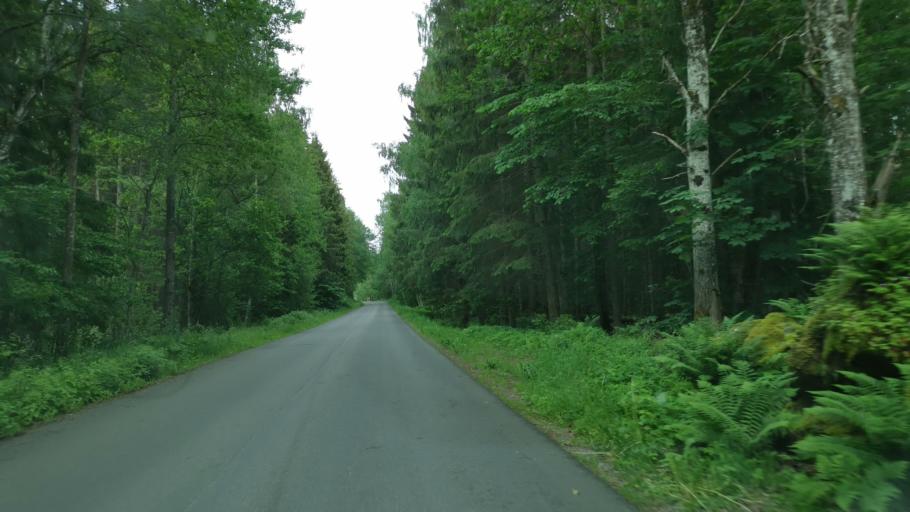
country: SE
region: Vaestra Goetaland
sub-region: Vanersborgs Kommun
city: Vargon
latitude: 58.3587
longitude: 12.3672
